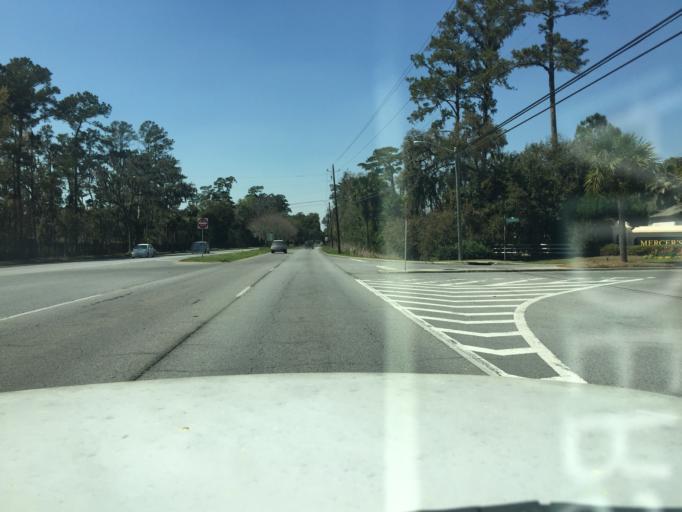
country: US
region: Georgia
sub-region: Chatham County
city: Whitemarsh Island
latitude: 32.0369
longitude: -81.0130
